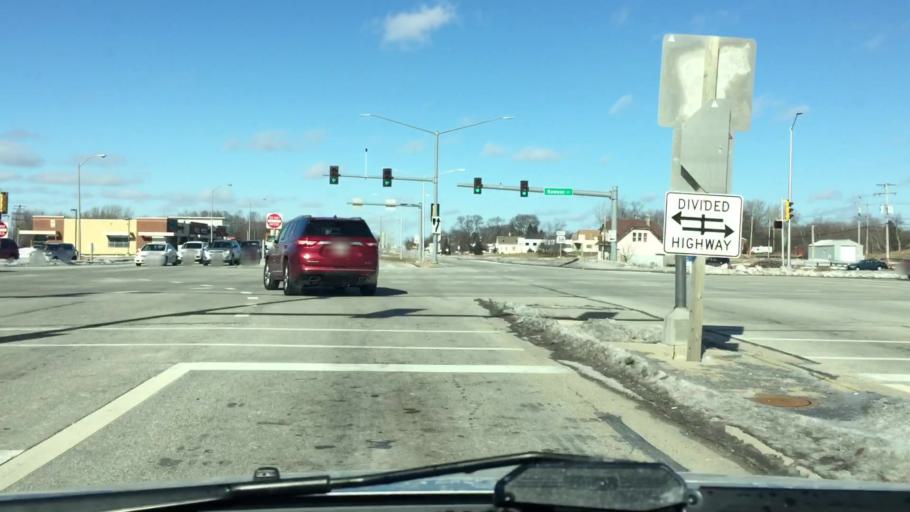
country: US
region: Wisconsin
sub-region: Milwaukee County
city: South Milwaukee
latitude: 42.9154
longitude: -87.9109
